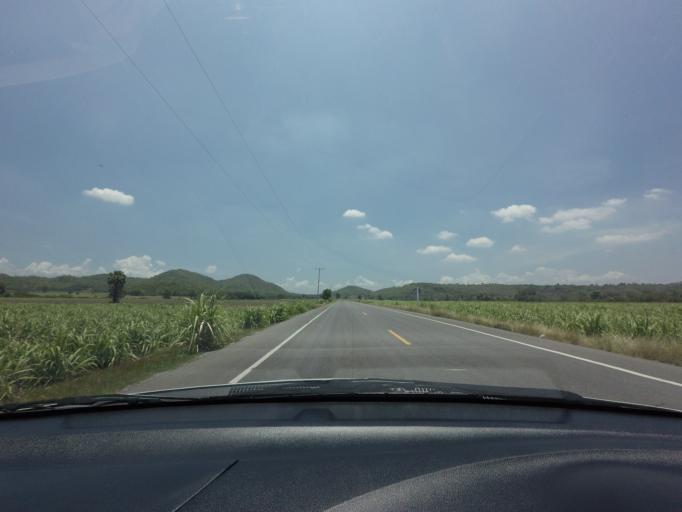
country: TH
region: Suphan Buri
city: Dan Chang
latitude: 14.9053
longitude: 99.7098
